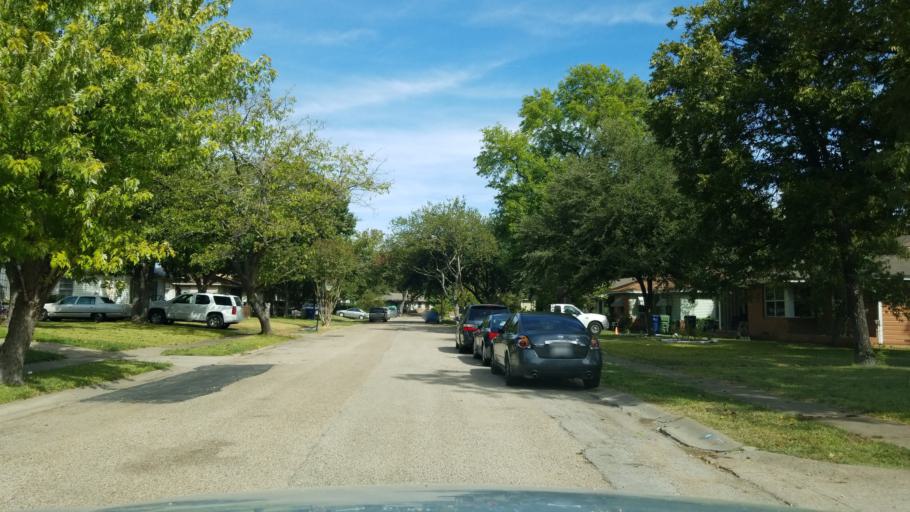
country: US
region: Texas
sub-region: Dallas County
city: Garland
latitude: 32.9016
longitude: -96.6558
